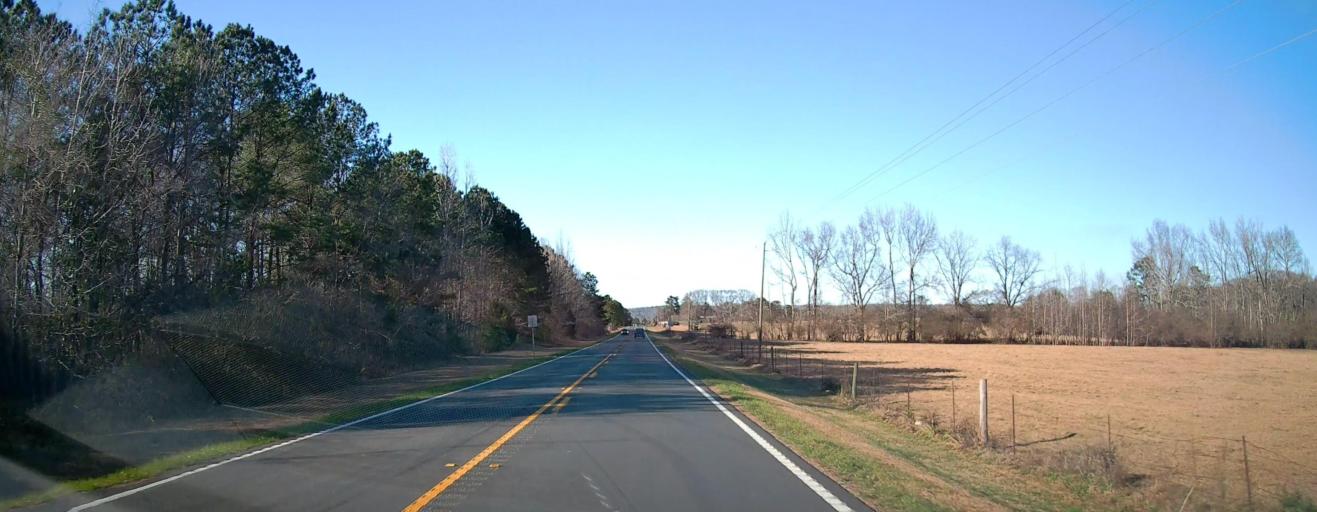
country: US
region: Georgia
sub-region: Talbot County
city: Sardis
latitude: 32.8133
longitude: -84.6972
